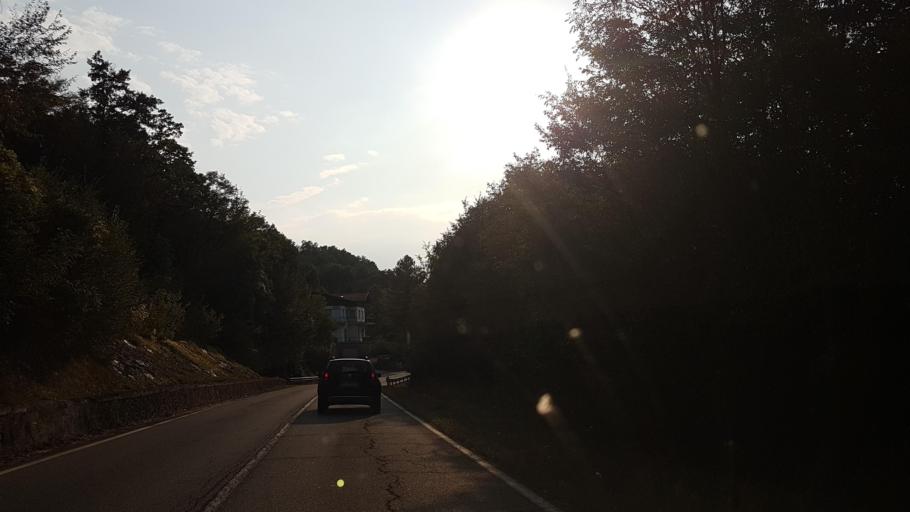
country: IT
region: Emilia-Romagna
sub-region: Provincia di Parma
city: Solignano
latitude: 44.6149
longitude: 9.9946
